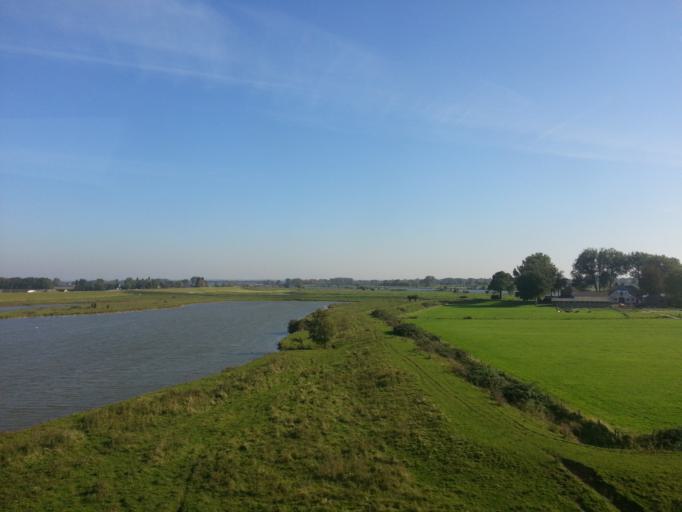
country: NL
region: Gelderland
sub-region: Gemeente Culemborg
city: Culemborg
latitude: 51.9637
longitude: 5.2105
